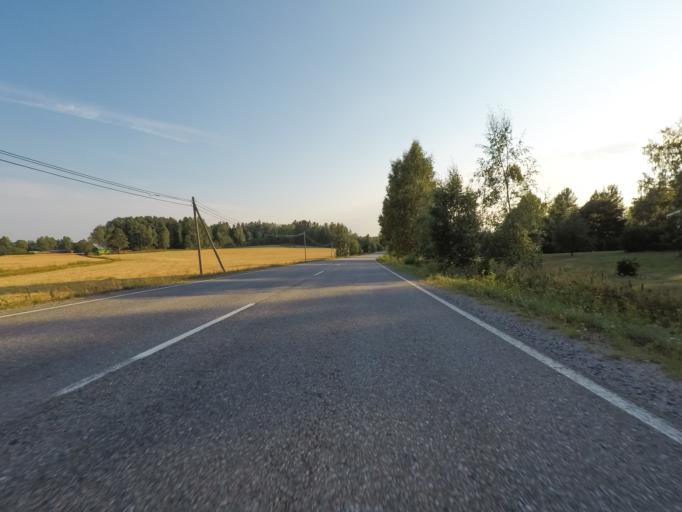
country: FI
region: Uusimaa
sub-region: Helsinki
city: Karjalohja
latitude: 60.2622
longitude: 23.7574
